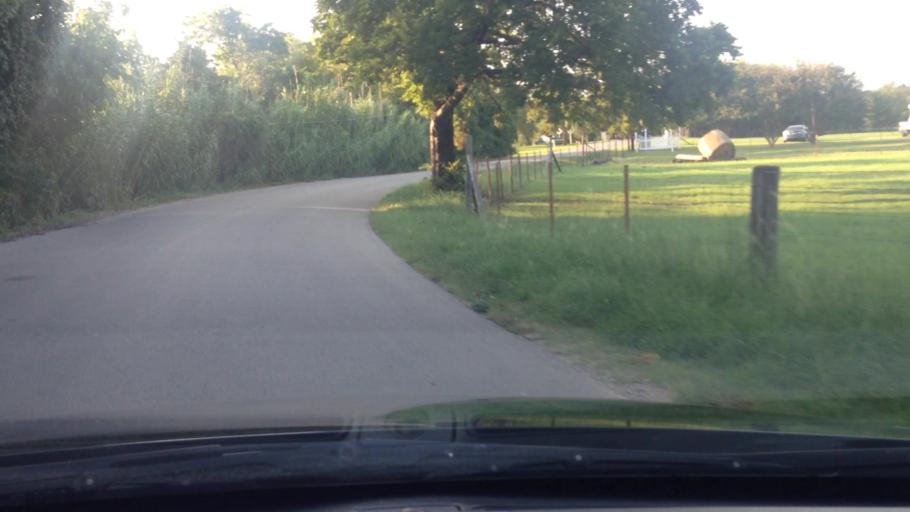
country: US
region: Texas
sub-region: Tarrant County
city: Rendon
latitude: 32.5838
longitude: -97.2499
